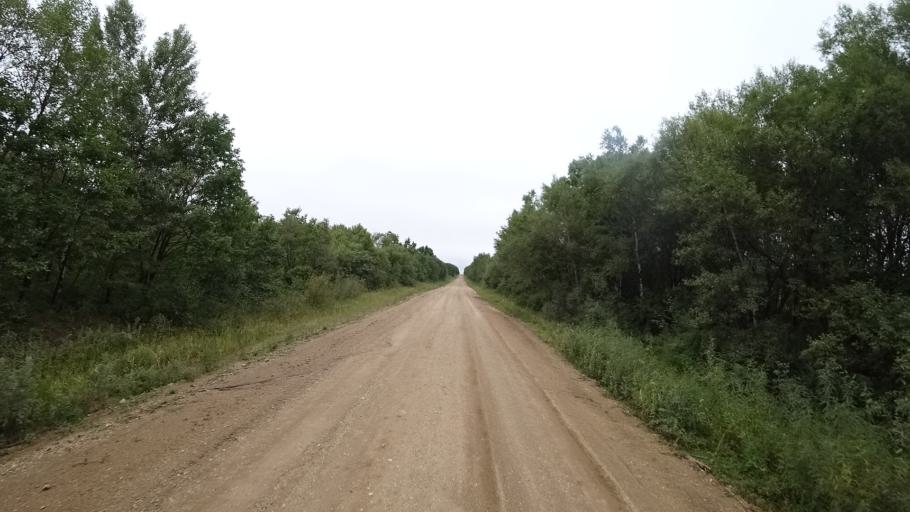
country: RU
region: Primorskiy
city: Ivanovka
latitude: 44.0250
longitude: 132.5243
